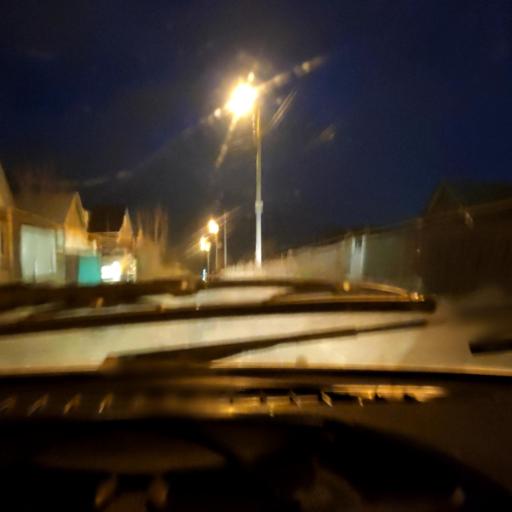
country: RU
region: Samara
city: Zhigulevsk
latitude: 53.4826
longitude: 49.5276
